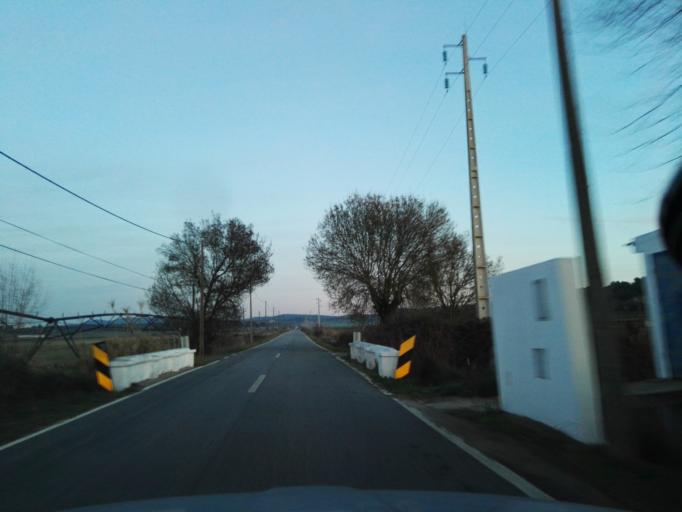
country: PT
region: Evora
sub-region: Arraiolos
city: Arraiolos
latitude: 38.7624
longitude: -8.1170
